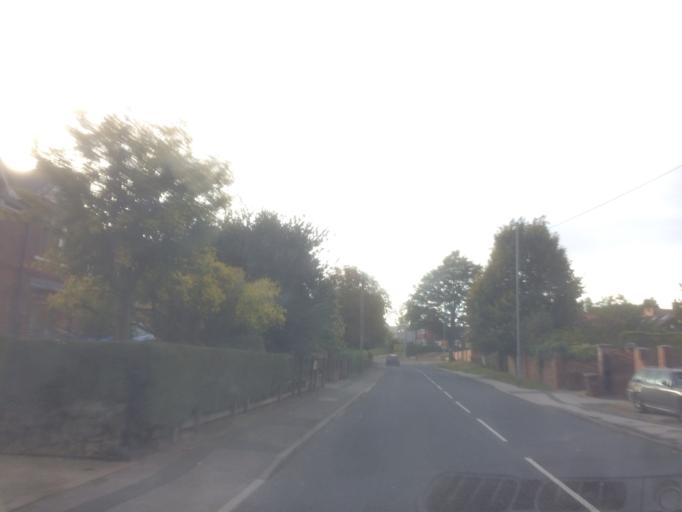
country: GB
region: England
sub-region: City and Borough of Wakefield
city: Pontefract
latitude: 53.7179
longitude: -1.3115
